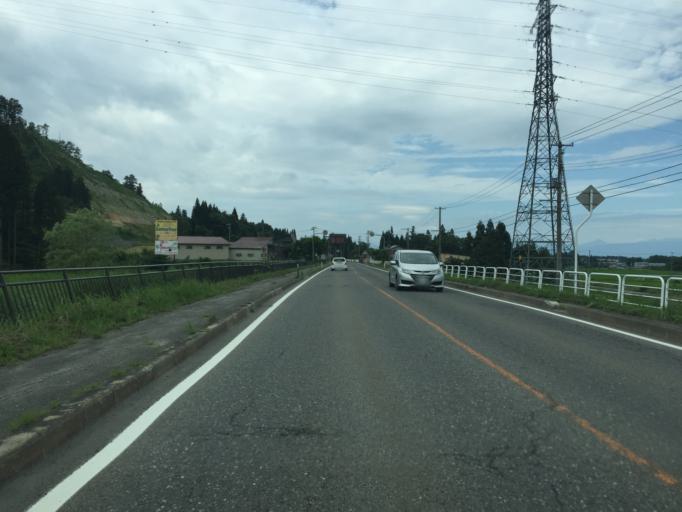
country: JP
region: Yamagata
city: Yonezawa
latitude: 37.8917
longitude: 140.1707
